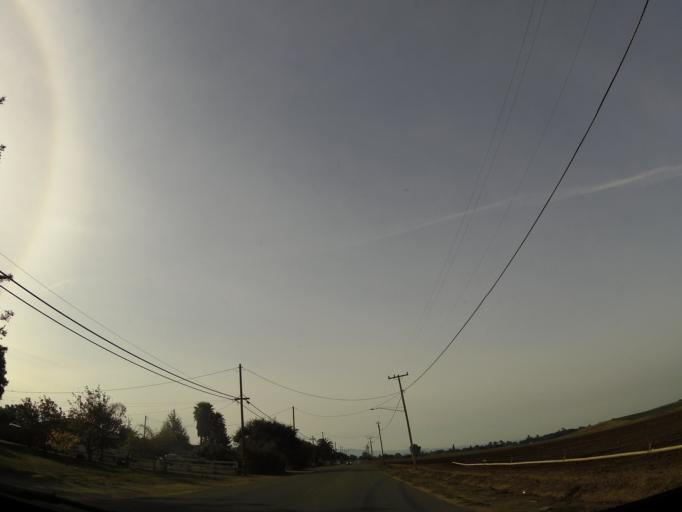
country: US
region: California
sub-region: Monterey County
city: Prunedale
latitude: 36.7583
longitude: -121.6168
